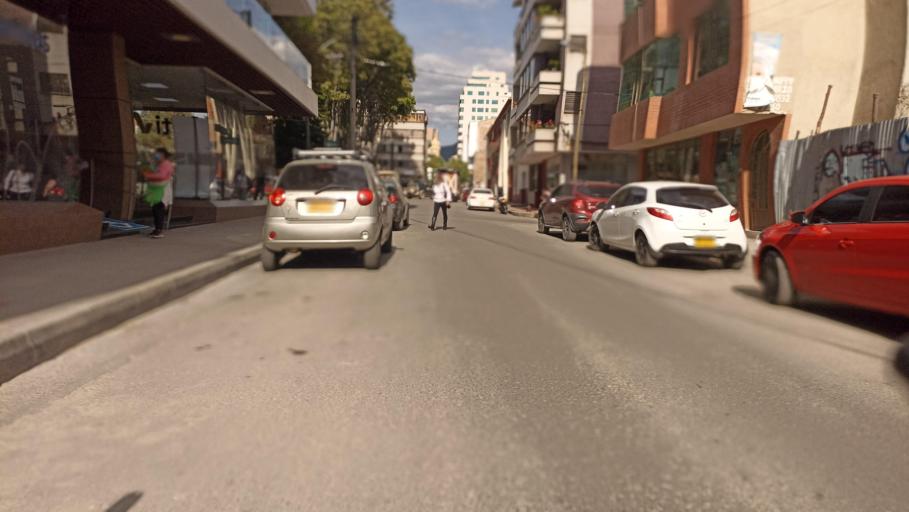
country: CO
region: Boyaca
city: Duitama
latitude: 5.8266
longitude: -73.0367
